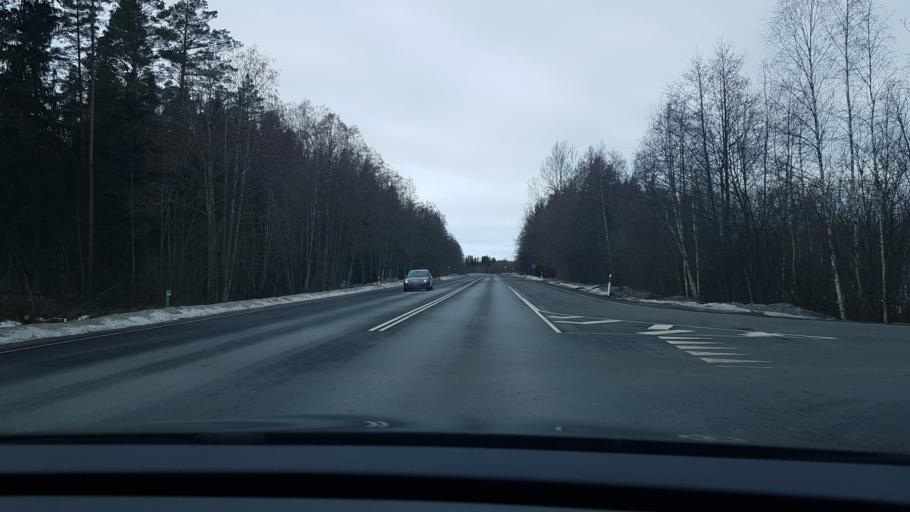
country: EE
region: Paernumaa
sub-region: Paikuse vald
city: Paikuse
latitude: 58.2584
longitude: 24.6738
